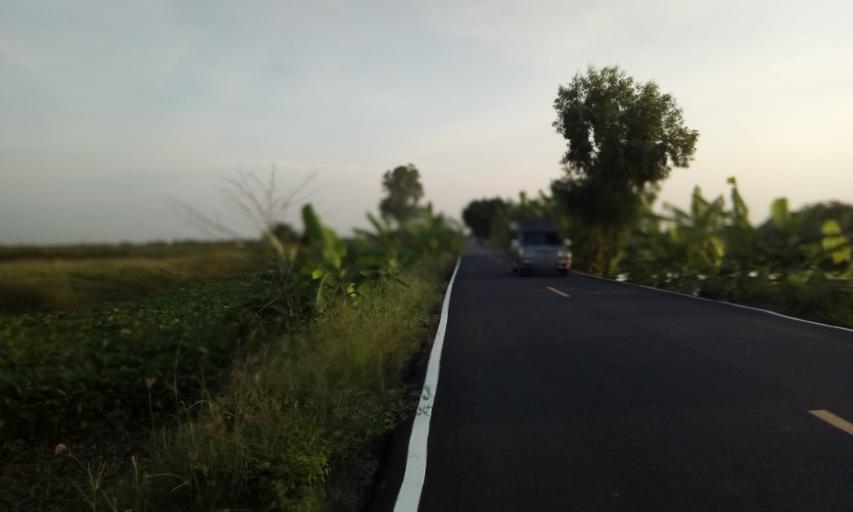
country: TH
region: Pathum Thani
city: Nong Suea
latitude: 14.0437
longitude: 100.8570
